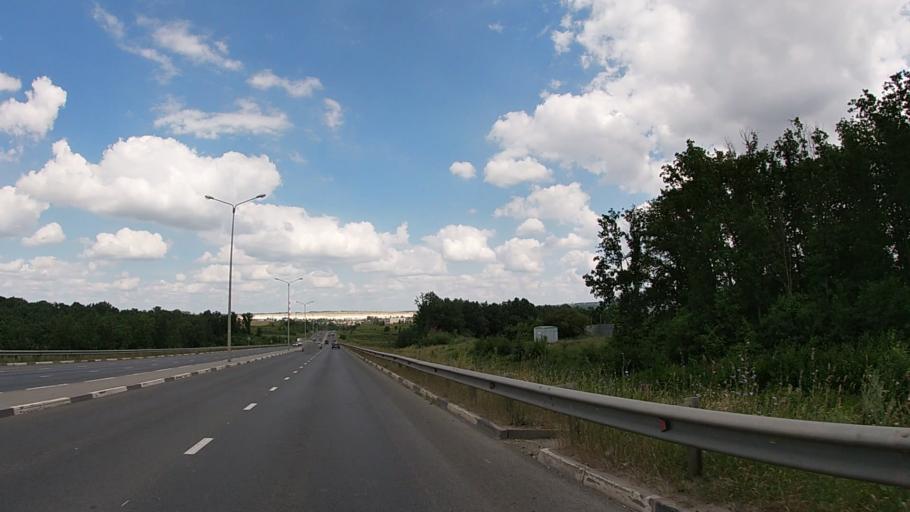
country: RU
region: Belgorod
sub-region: Belgorodskiy Rayon
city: Belgorod
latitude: 50.5976
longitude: 36.5304
